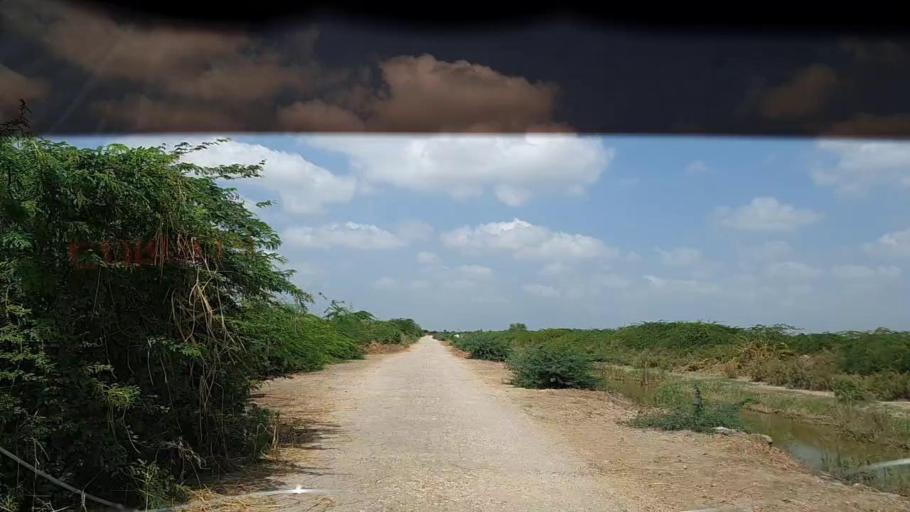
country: PK
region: Sindh
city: Kadhan
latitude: 24.5851
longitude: 68.9700
